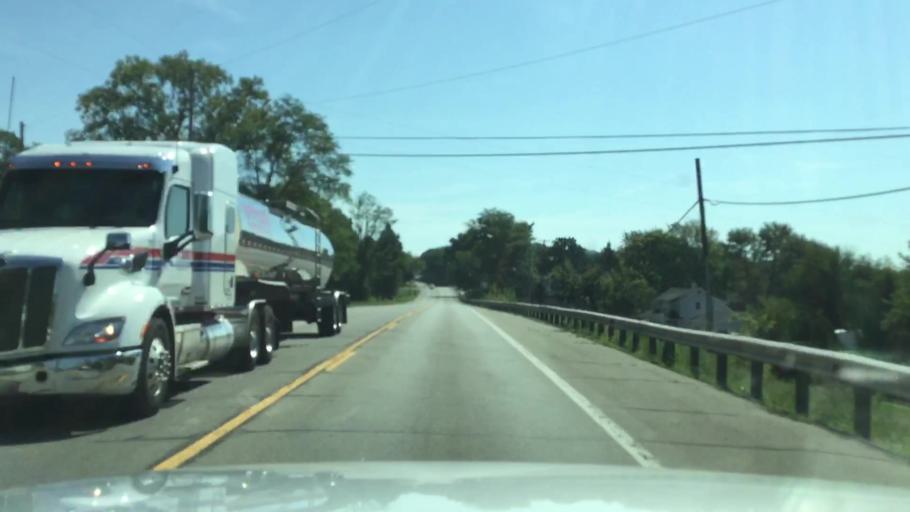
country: US
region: Michigan
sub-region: Lenawee County
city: Manitou Beach-Devils Lake
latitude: 42.0071
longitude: -84.2900
